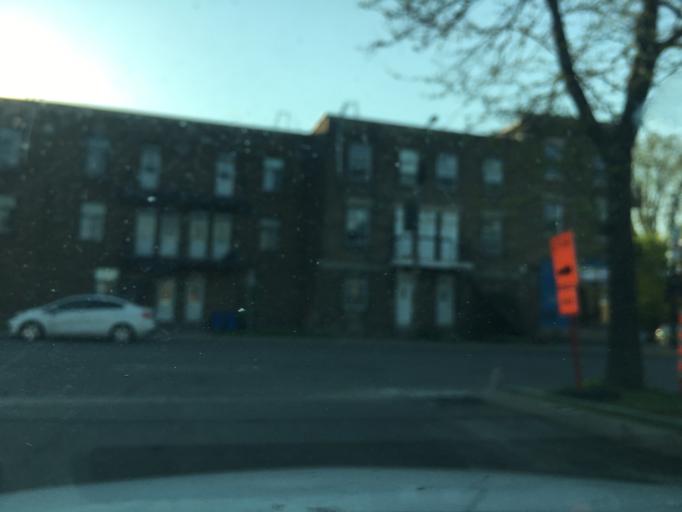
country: CA
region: Quebec
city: Westmount
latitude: 45.4708
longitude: -73.5639
